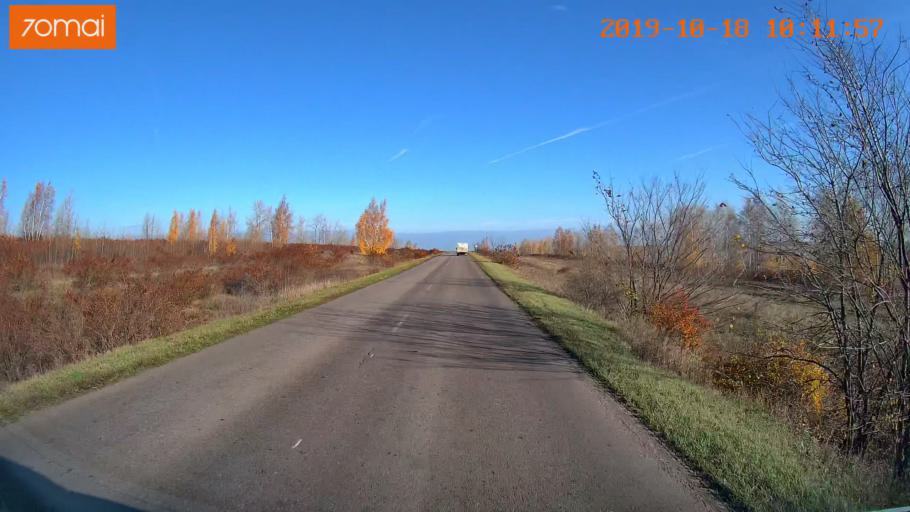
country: RU
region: Tula
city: Kurkino
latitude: 53.3882
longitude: 38.5039
